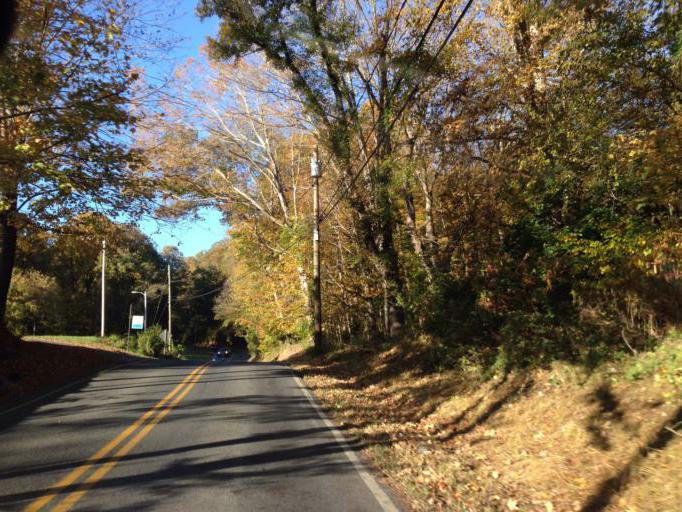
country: US
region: Maryland
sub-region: Carroll County
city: Sykesville
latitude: 39.3615
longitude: -76.9697
